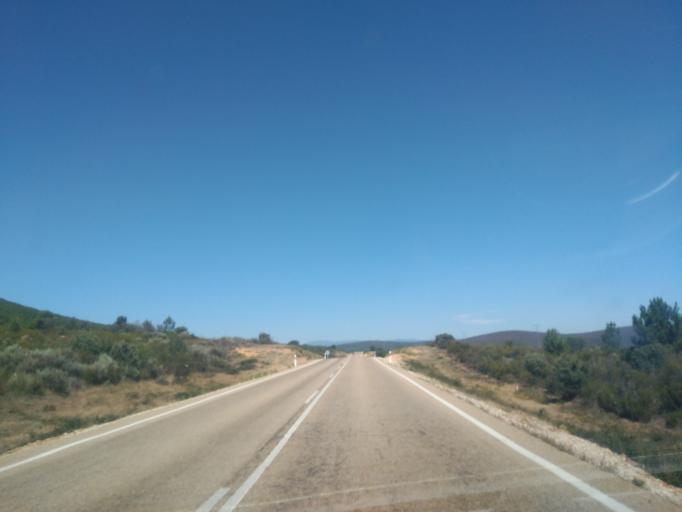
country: ES
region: Castille and Leon
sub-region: Provincia de Zamora
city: Ferreras de Abajo
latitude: 41.8800
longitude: -6.0177
